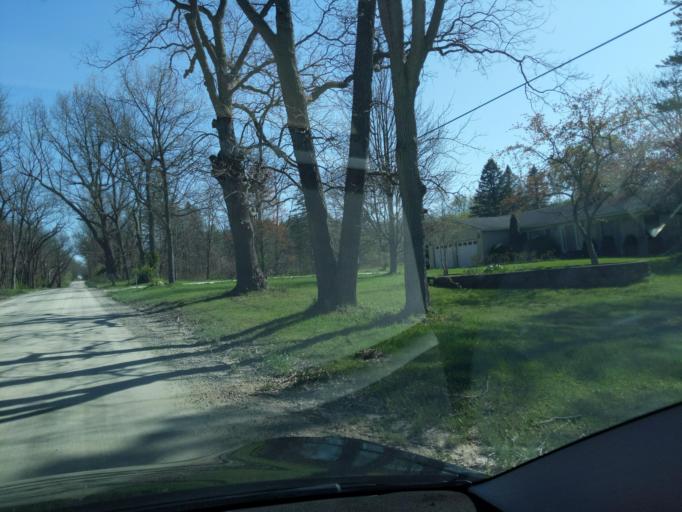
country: US
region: Michigan
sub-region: Washtenaw County
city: Chelsea
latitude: 42.3923
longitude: -84.0837
